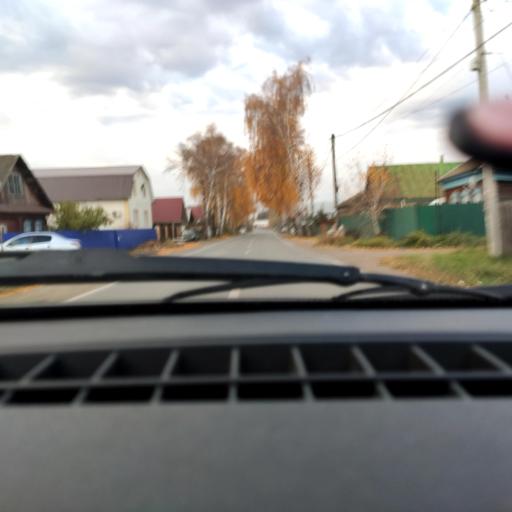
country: RU
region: Bashkortostan
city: Iglino
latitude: 54.8301
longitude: 56.1889
